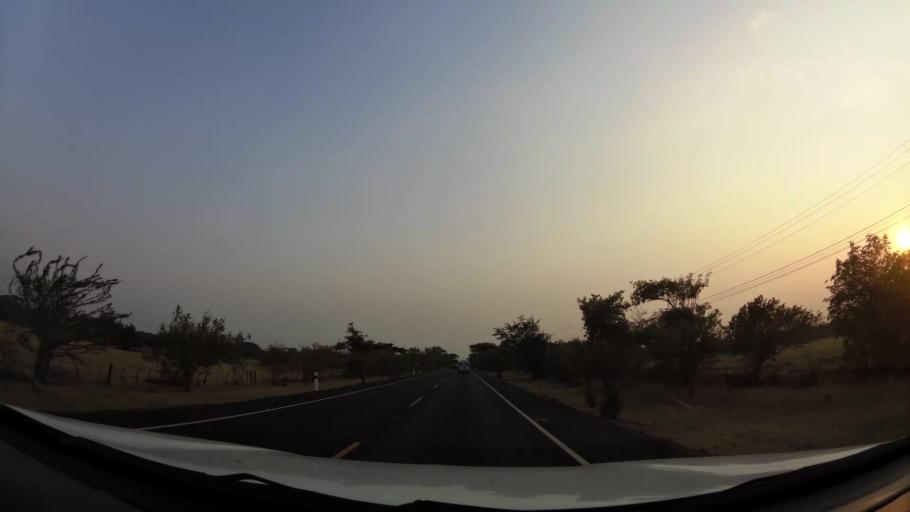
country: NI
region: Leon
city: La Paz Centro
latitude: 12.3086
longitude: -86.7038
